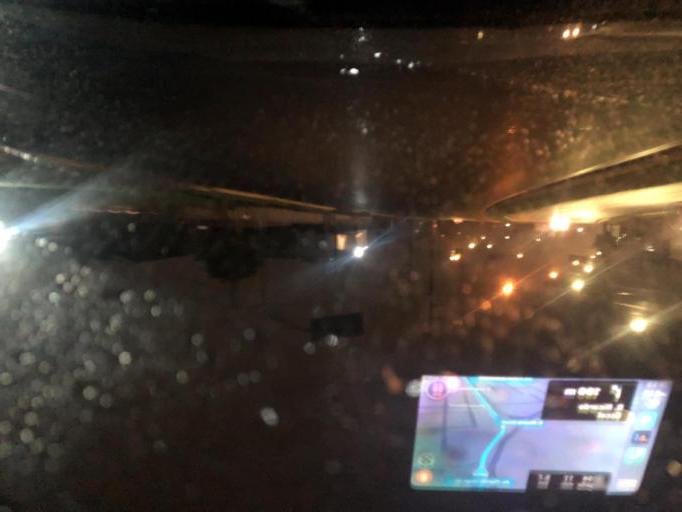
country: BR
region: Santa Catarina
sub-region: Joinville
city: Joinville
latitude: -26.3706
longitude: -48.8321
